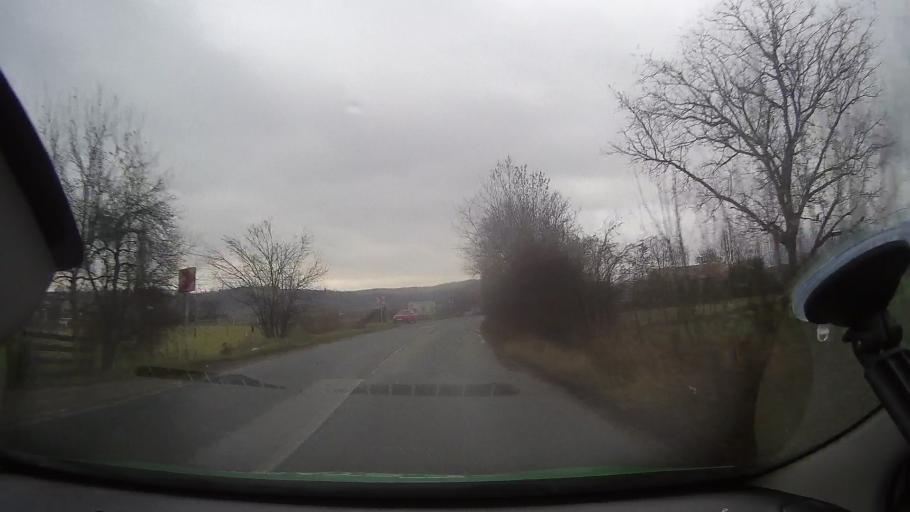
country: RO
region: Arad
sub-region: Comuna Halmagiu
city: Halmagiu
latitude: 46.2670
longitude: 22.5973
